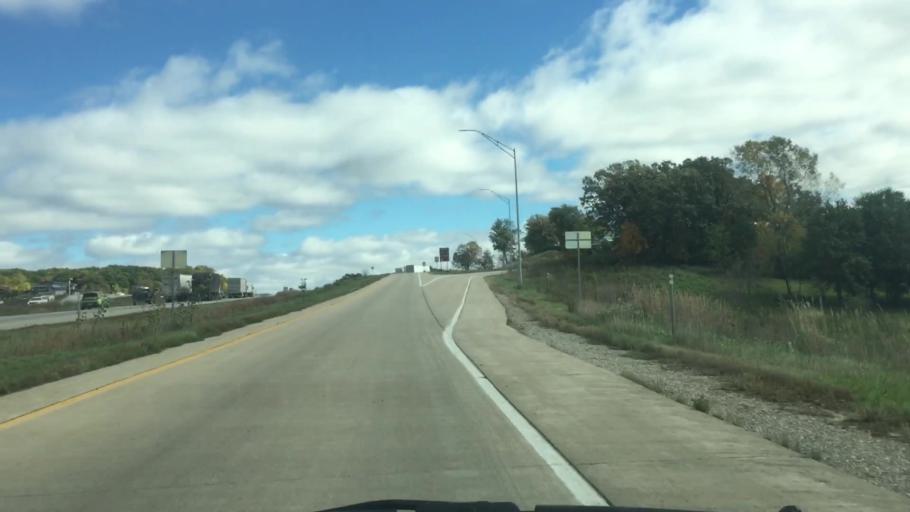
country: US
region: Iowa
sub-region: Poweshiek County
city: Grinnell
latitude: 41.6951
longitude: -92.7776
